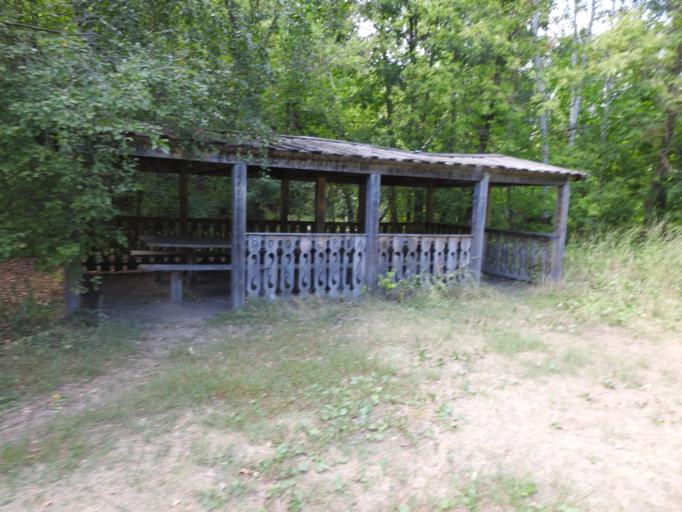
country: RU
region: Saratov
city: Kamenskiy
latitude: 50.4922
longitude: 45.7010
